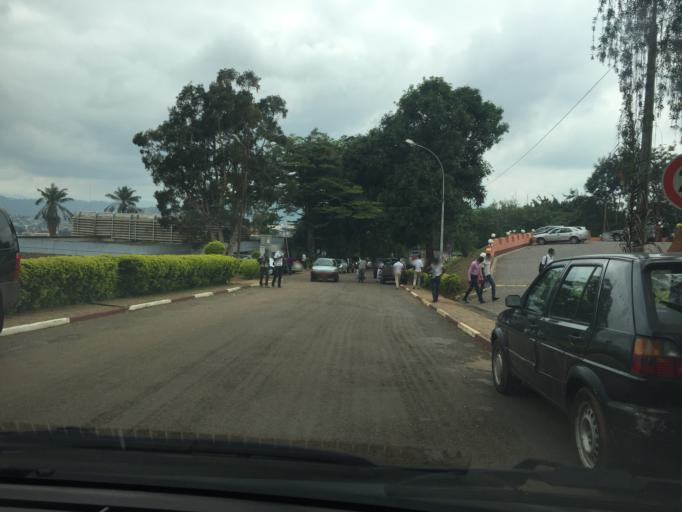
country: CM
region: Centre
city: Yaounde
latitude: 3.8562
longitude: 11.5026
